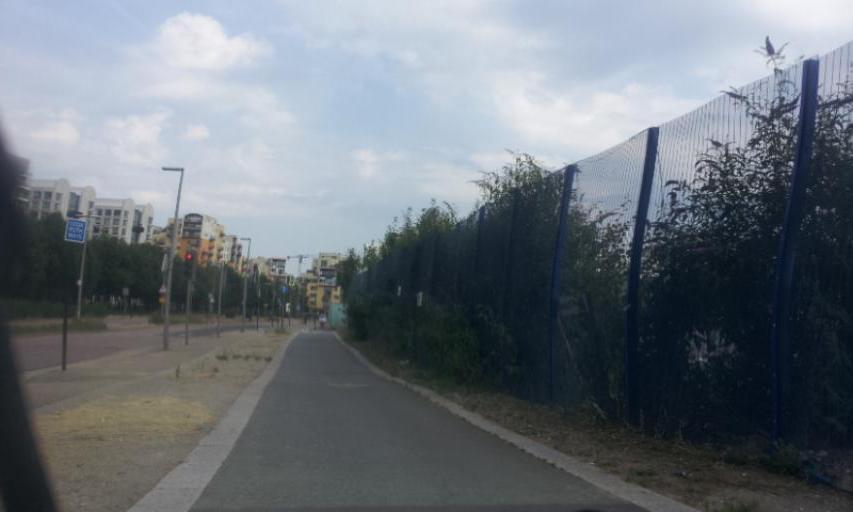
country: GB
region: England
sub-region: Greater London
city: Poplar
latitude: 51.4962
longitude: 0.0089
